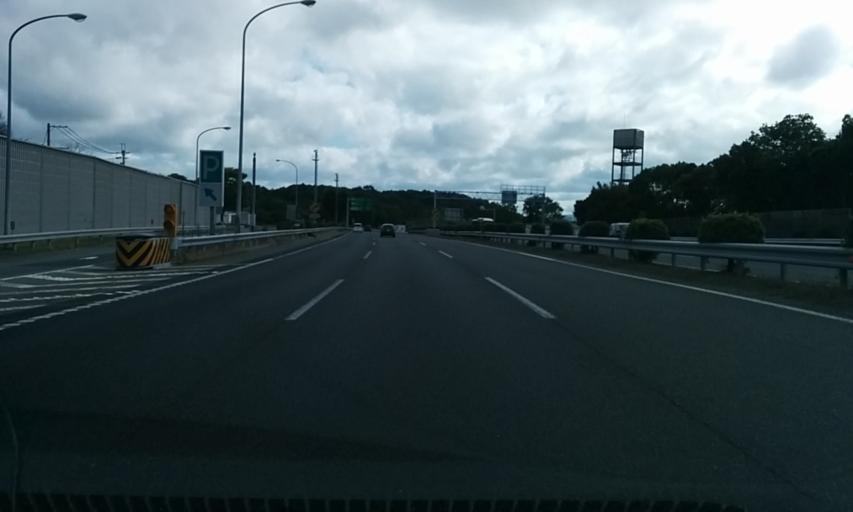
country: JP
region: Hyogo
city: Sandacho
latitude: 34.8851
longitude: 135.1676
